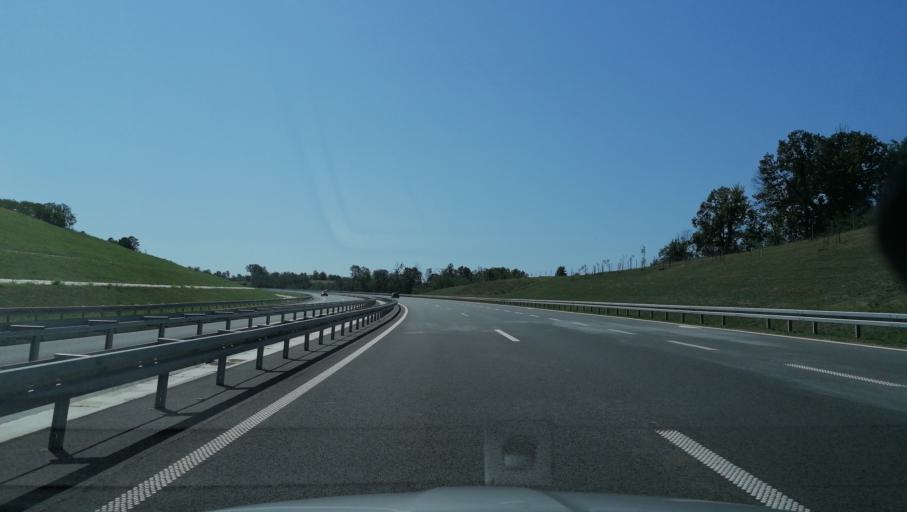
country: RS
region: Central Serbia
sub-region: Kolubarski Okrug
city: Ub
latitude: 44.4816
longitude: 20.1144
